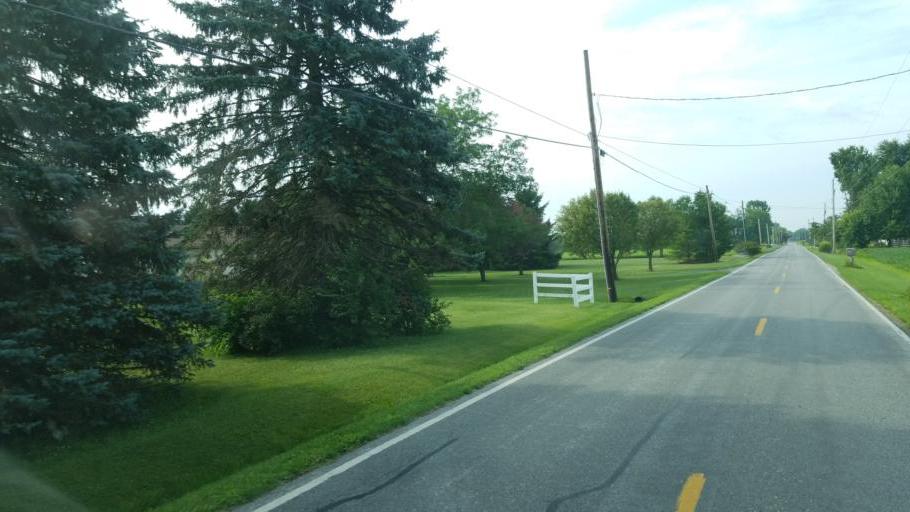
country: US
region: Ohio
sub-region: Union County
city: New California
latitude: 40.2147
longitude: -83.1675
